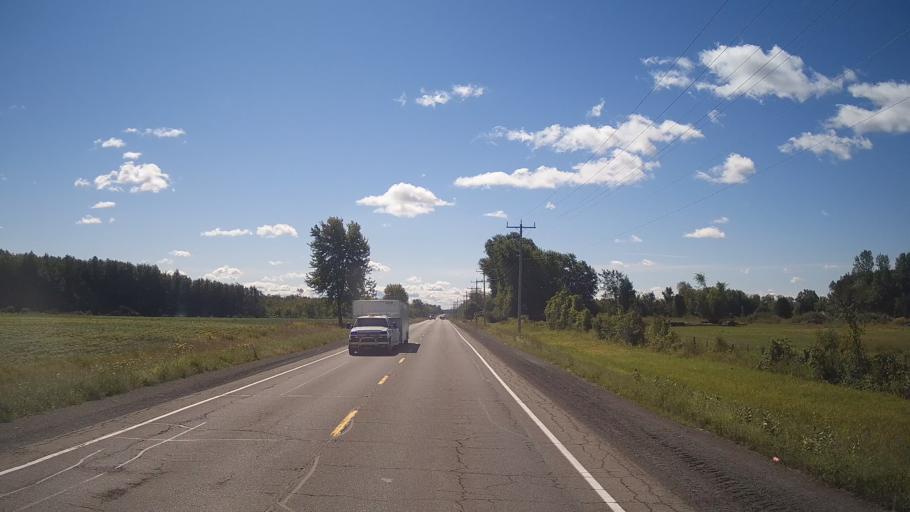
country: US
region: New York
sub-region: St. Lawrence County
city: Norfolk
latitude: 44.9555
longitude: -75.2280
